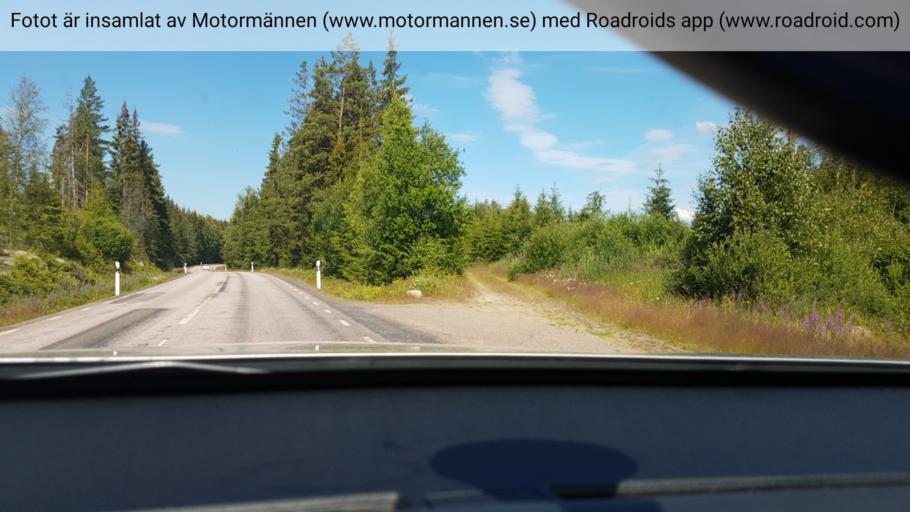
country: SE
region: Vaermland
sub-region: Sunne Kommun
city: Sunne
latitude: 59.8663
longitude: 13.2709
